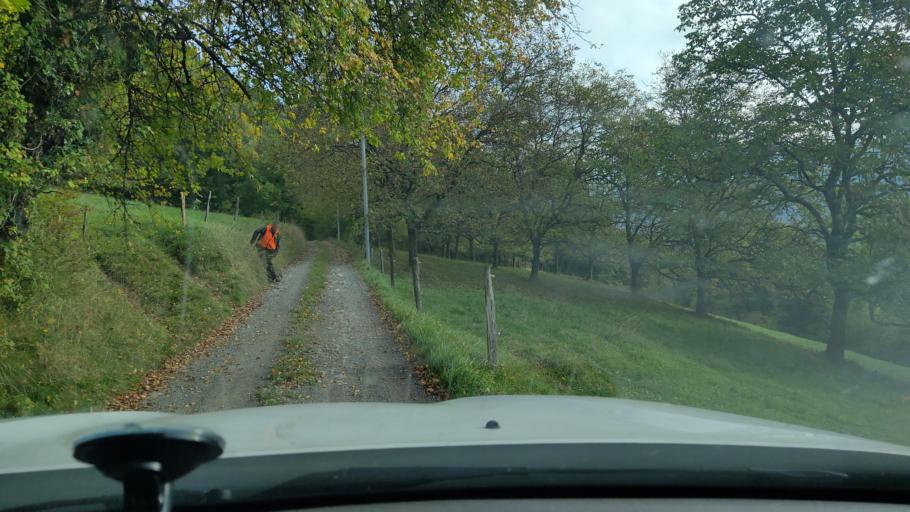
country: FR
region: Rhone-Alpes
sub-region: Departement de la Savoie
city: La Rochette
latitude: 45.4818
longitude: 6.1225
